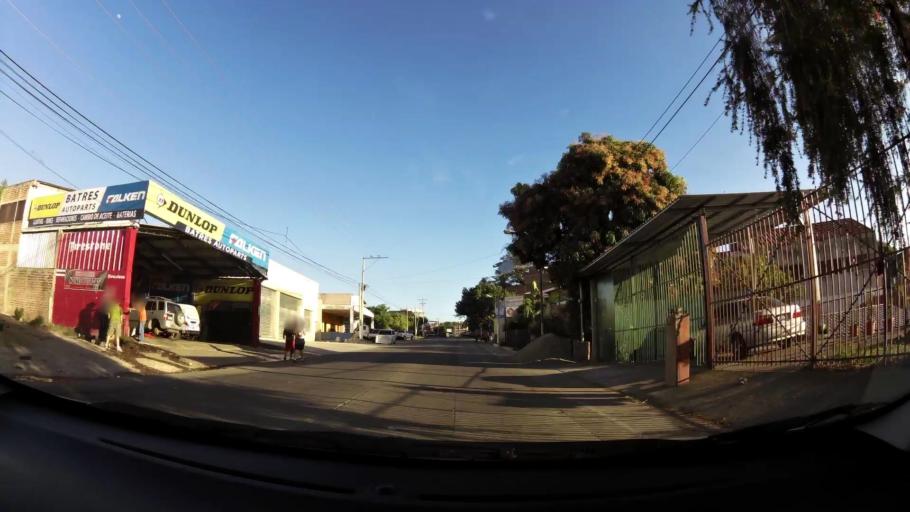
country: SV
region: Santa Ana
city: Metapan
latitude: 14.3353
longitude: -89.4457
